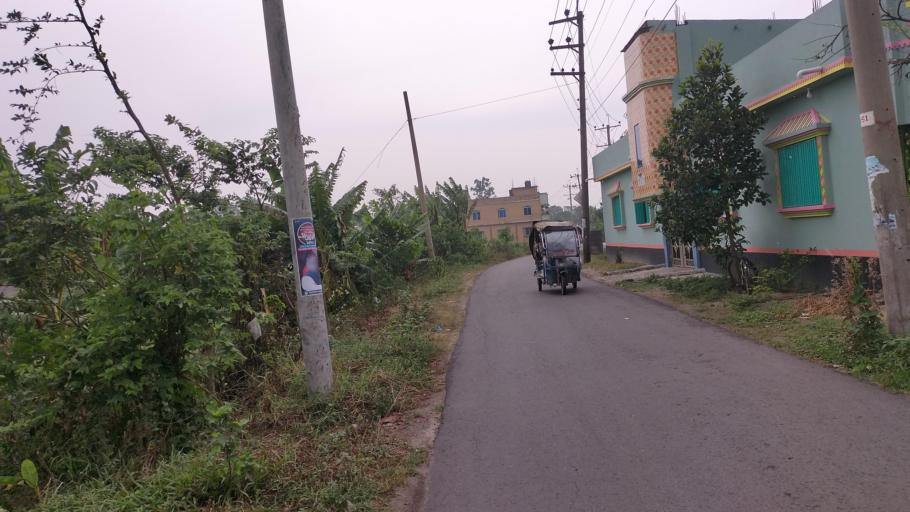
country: BD
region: Dhaka
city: Azimpur
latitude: 23.6797
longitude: 90.3491
